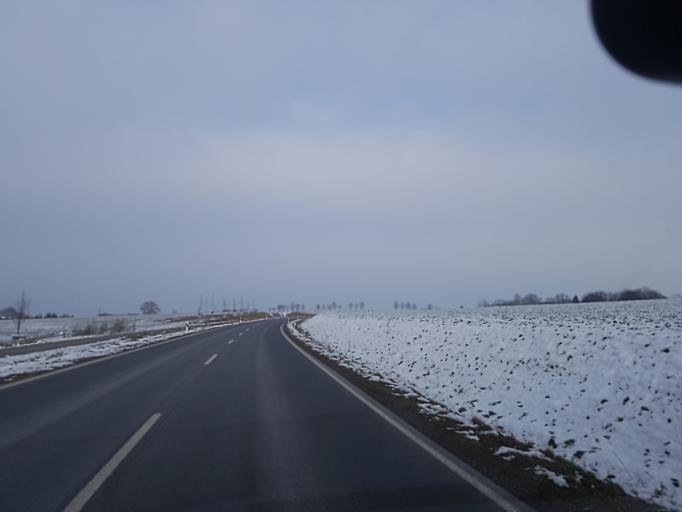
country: DE
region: Saxony
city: Leisnig
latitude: 51.1862
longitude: 12.9234
